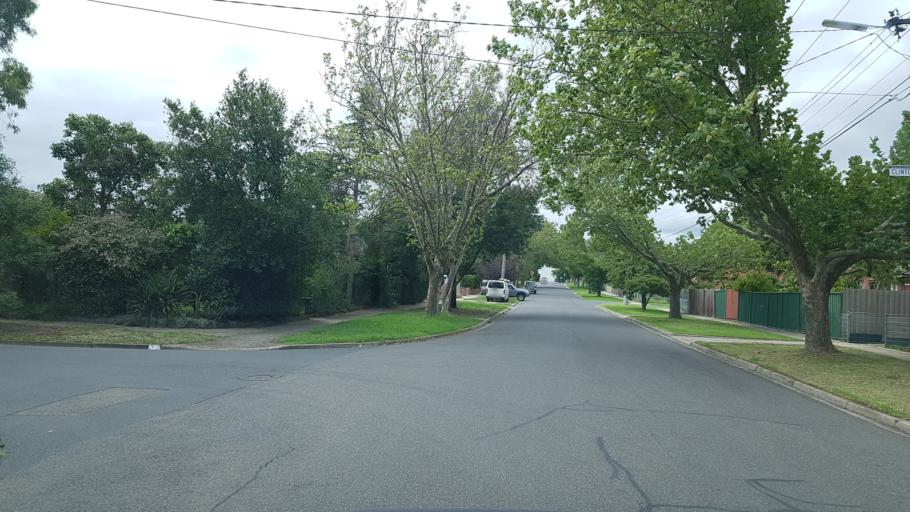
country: AU
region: Victoria
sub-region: Banyule
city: Heidelberg Heights
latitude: -37.7512
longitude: 145.0505
